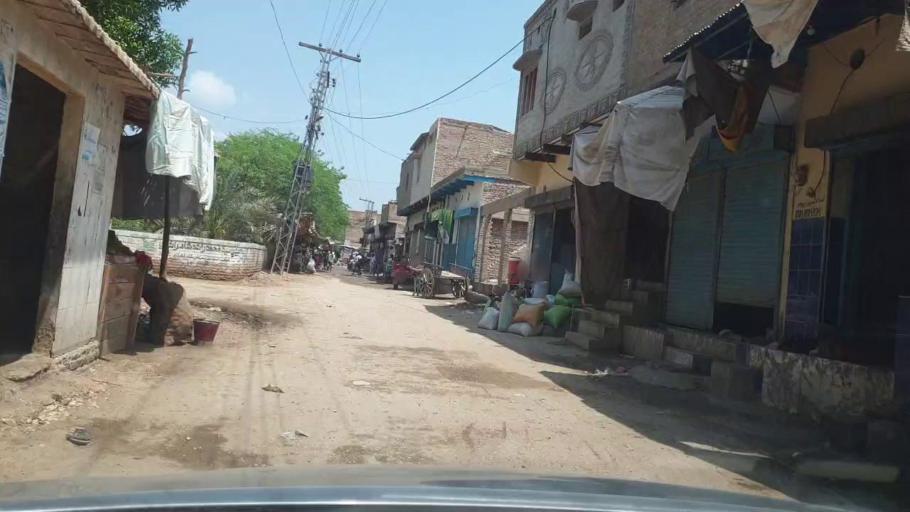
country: PK
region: Sindh
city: Pir jo Goth
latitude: 27.5940
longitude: 68.6139
